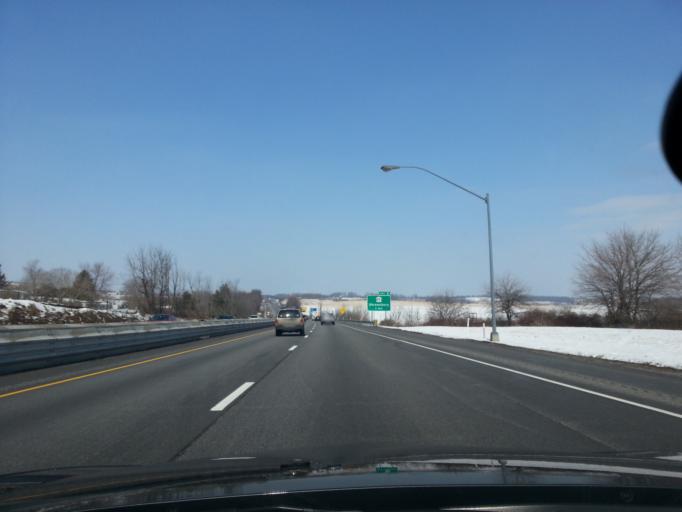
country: US
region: Pennsylvania
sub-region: York County
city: Shrewsbury
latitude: 39.7567
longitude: -76.6630
